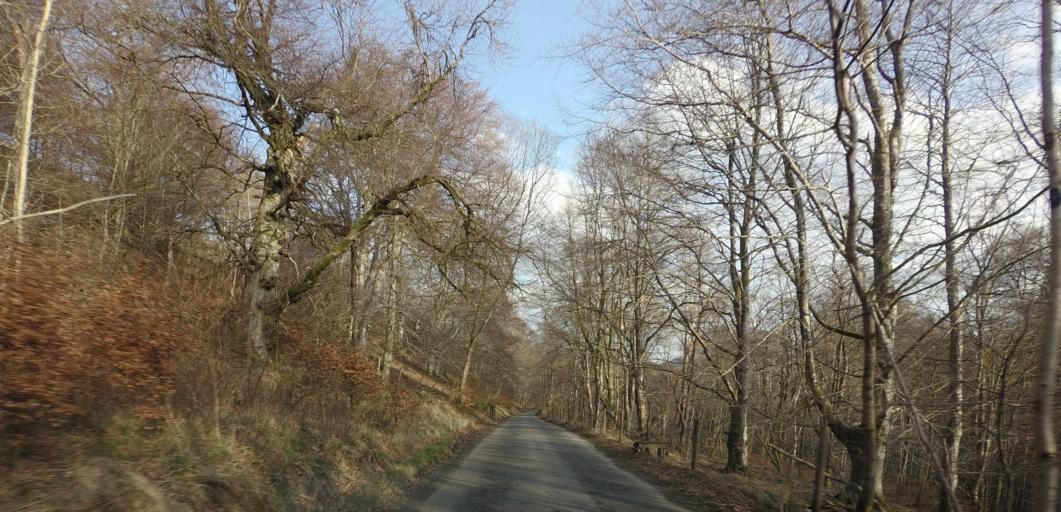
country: GB
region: Scotland
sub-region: Perth and Kinross
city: Aberfeldy
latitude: 56.6033
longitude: -4.0787
